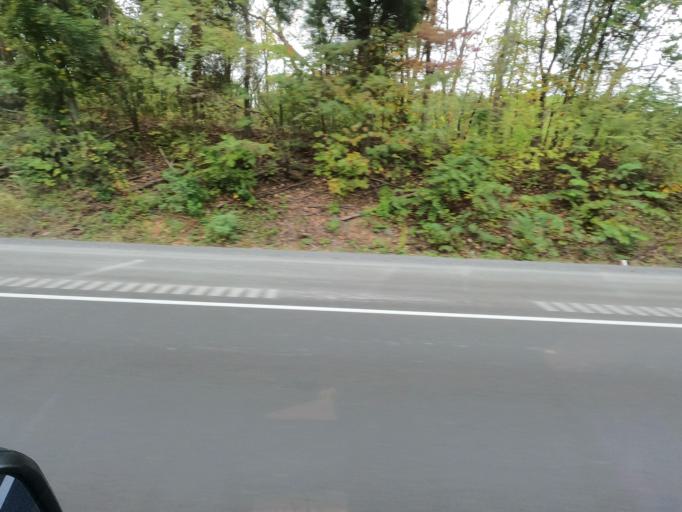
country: US
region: Tennessee
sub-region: Sullivan County
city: Colonial Heights
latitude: 36.5233
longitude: -82.5113
